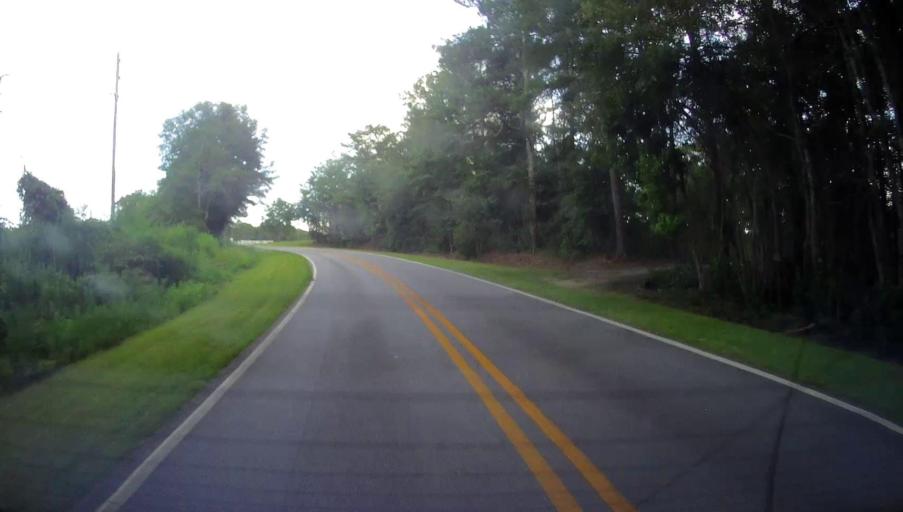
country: US
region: Georgia
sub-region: Crawford County
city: Knoxville
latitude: 32.7531
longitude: -83.9138
